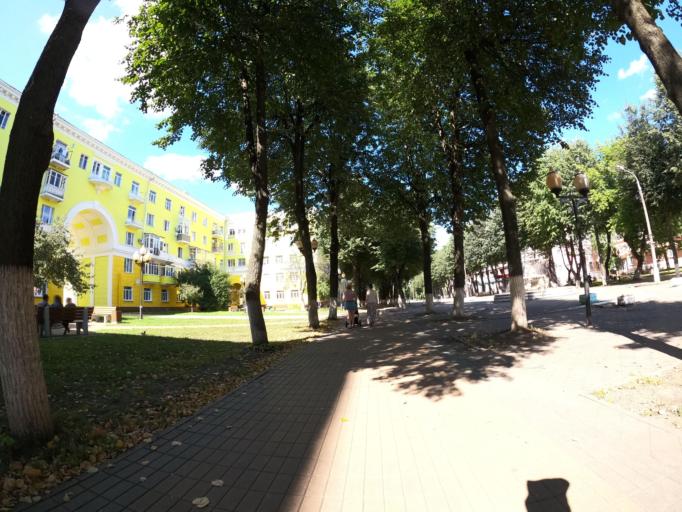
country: RU
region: Moskovskaya
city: Stupino
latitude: 54.8879
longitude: 38.0783
